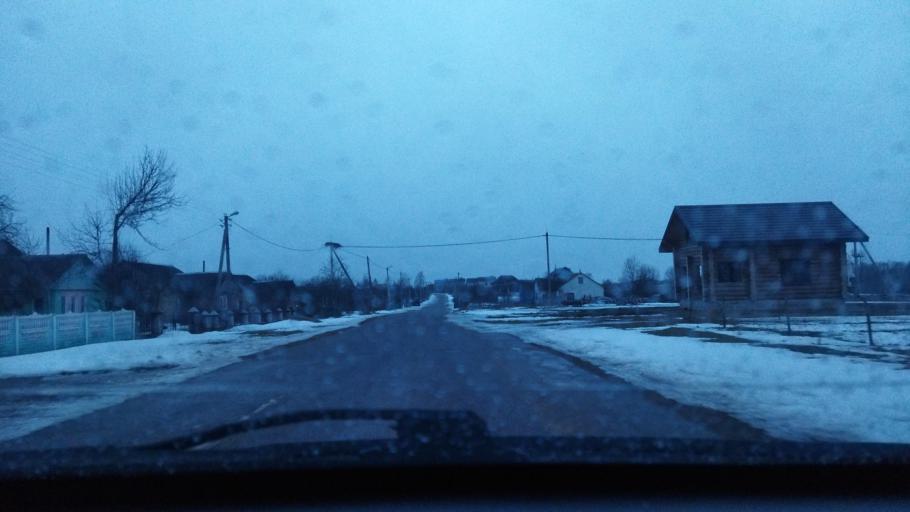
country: BY
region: Minsk
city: Svir
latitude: 54.8976
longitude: 26.3958
